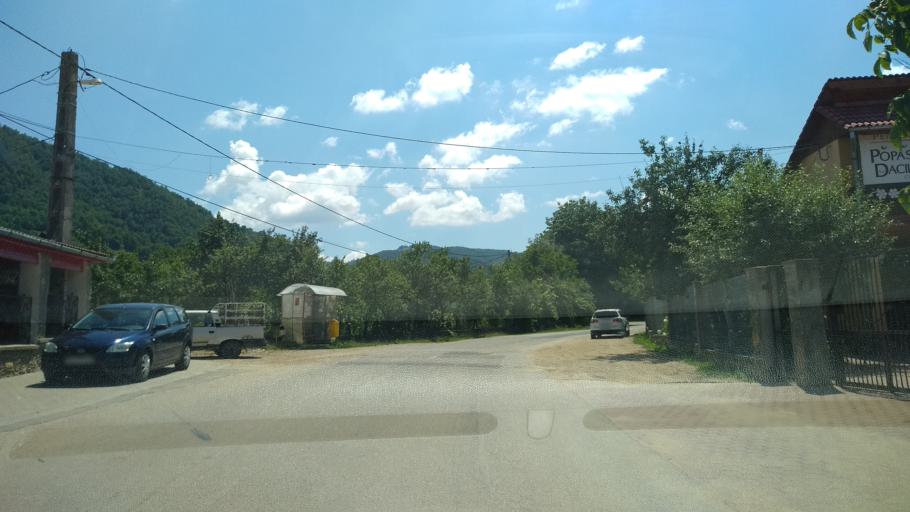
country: RO
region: Hunedoara
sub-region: Comuna Orastioara de Sus
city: Orastioara de Sus
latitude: 45.6954
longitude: 23.1619
